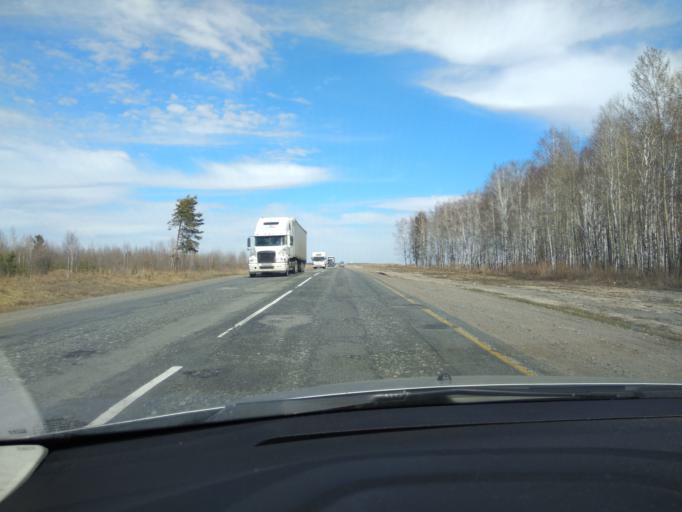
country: RU
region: Sverdlovsk
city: Pyshma
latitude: 56.9115
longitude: 63.1174
